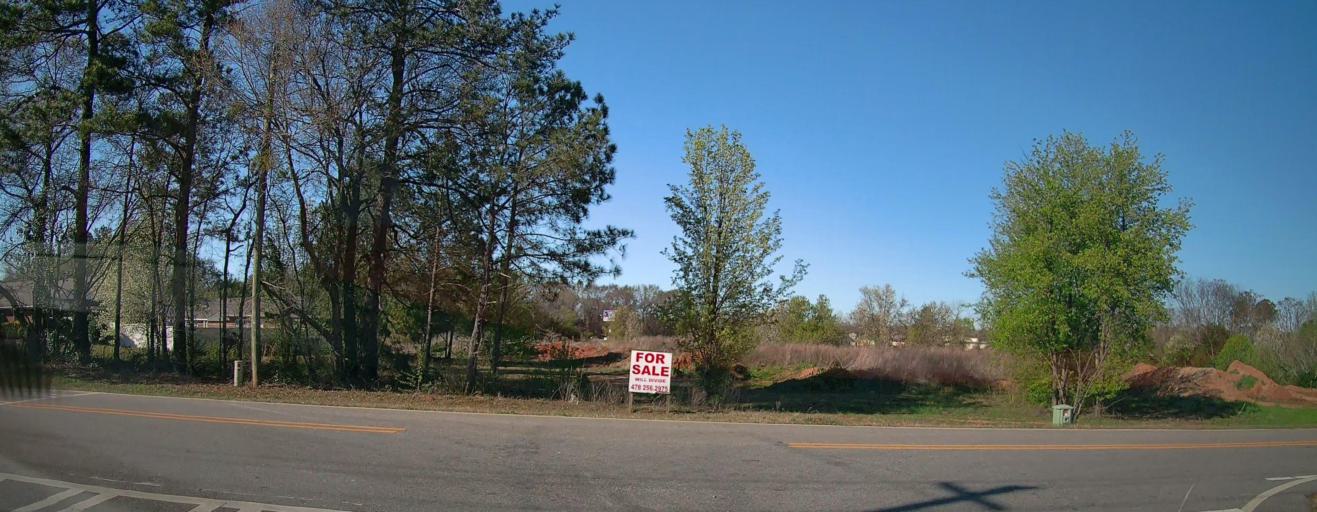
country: US
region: Georgia
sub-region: Peach County
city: Byron
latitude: 32.6515
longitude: -83.7532
